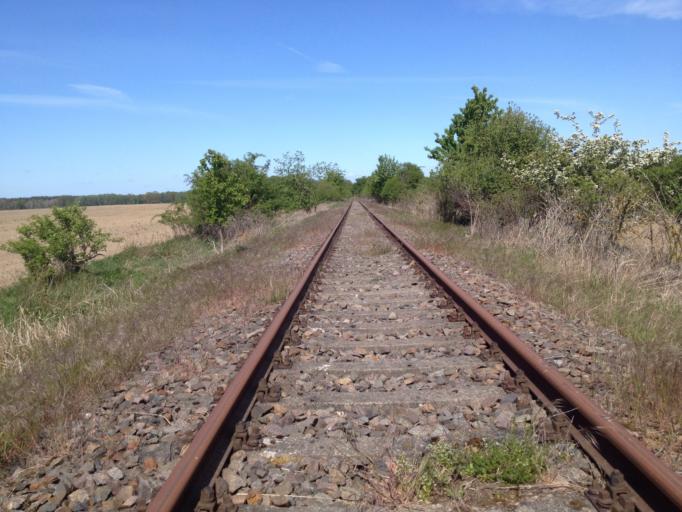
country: DE
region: Brandenburg
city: Templin
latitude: 53.1191
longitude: 13.4536
